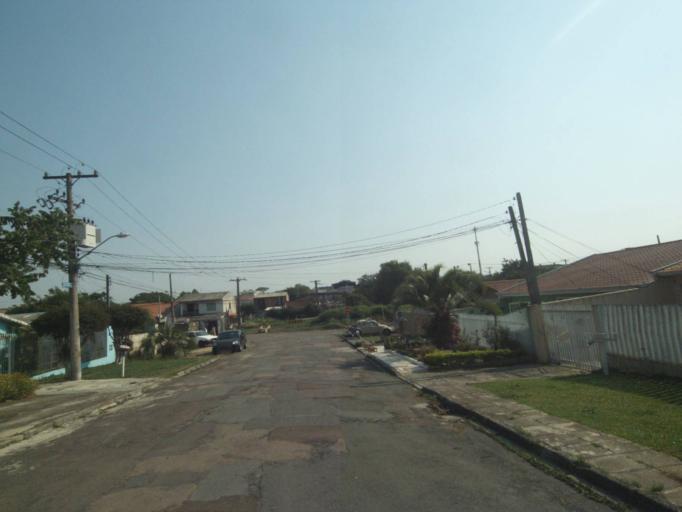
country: BR
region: Parana
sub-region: Sao Jose Dos Pinhais
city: Sao Jose dos Pinhais
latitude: -25.5075
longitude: -49.2767
